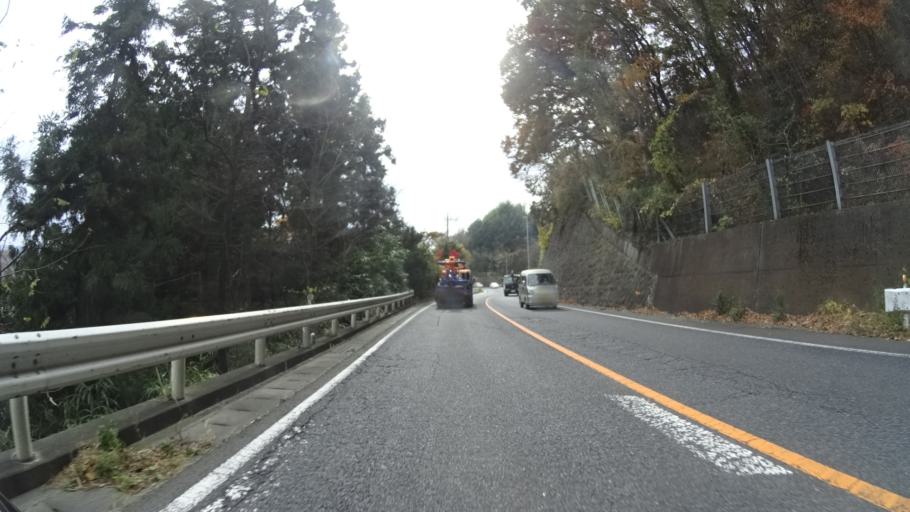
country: JP
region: Gunma
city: Numata
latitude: 36.5659
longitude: 139.0377
